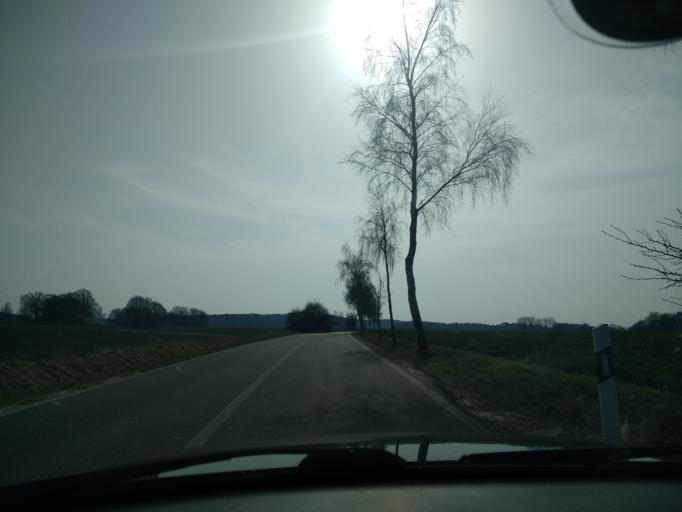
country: DE
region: Mecklenburg-Vorpommern
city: Bergen auf Ruegen
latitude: 54.4378
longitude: 13.4693
